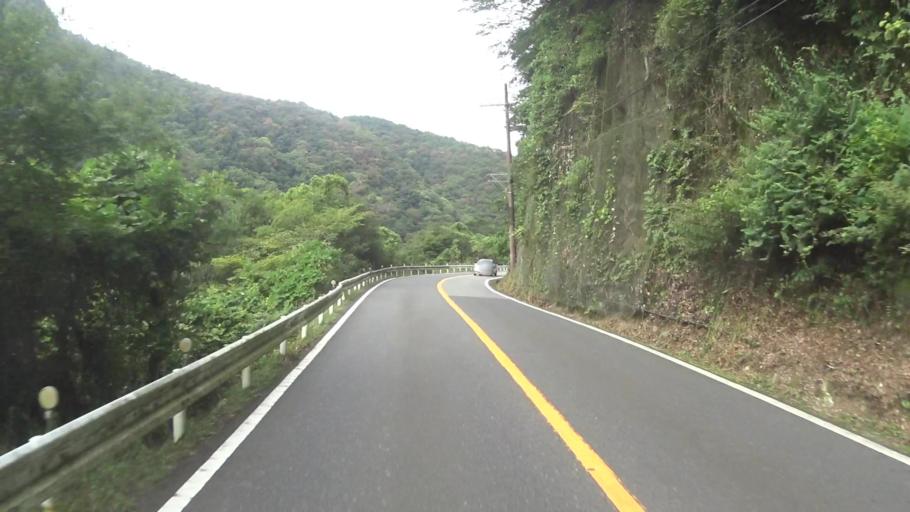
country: JP
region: Kyoto
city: Uji
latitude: 34.8791
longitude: 135.8477
